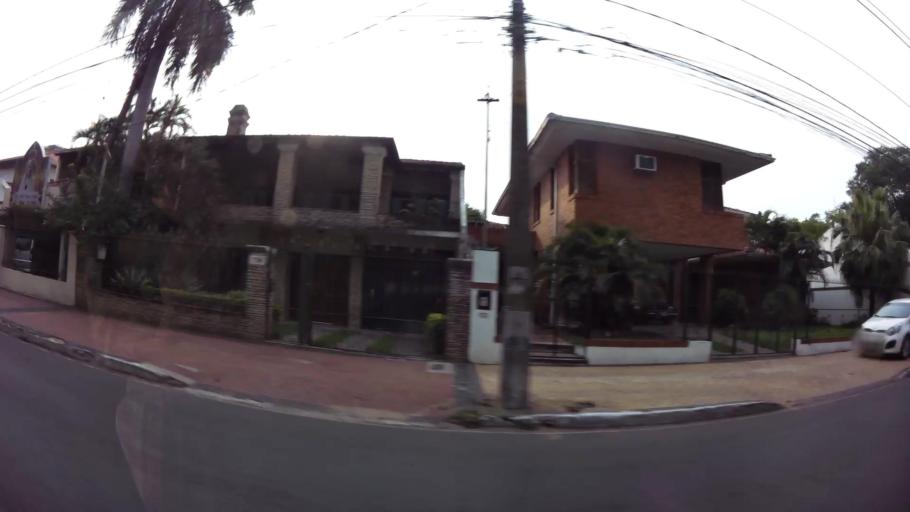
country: PY
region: Asuncion
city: Asuncion
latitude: -25.3009
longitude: -57.6060
